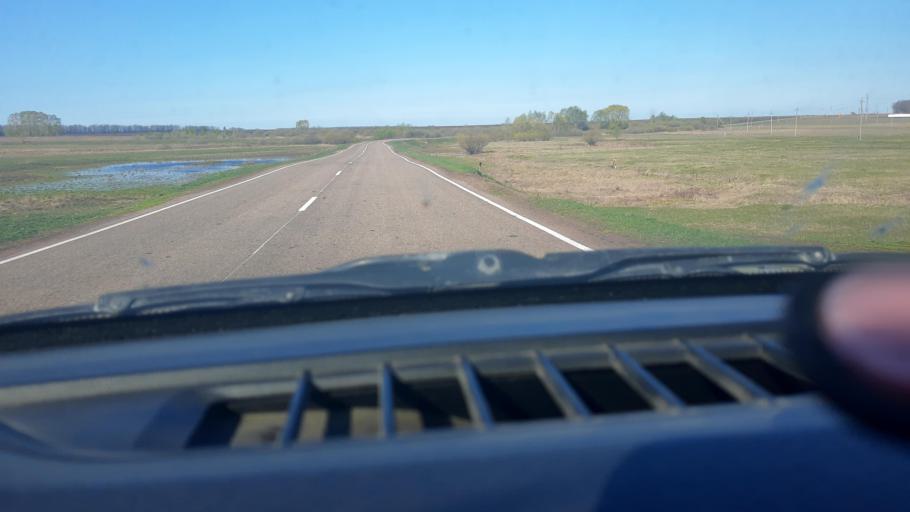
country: RU
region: Bashkortostan
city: Asanovo
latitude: 54.7641
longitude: 55.4769
